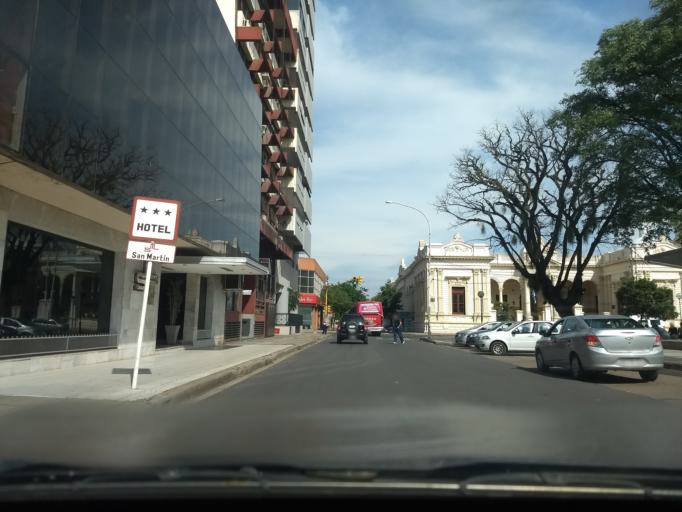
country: AR
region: Corrientes
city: Corrientes
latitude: -27.4688
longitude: -58.8305
